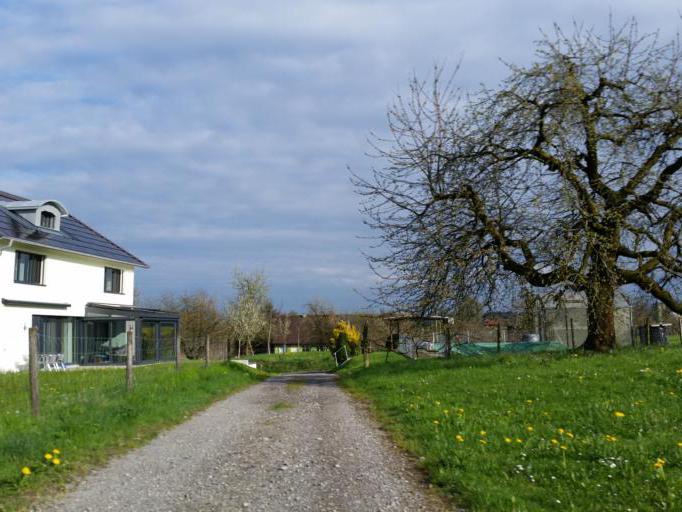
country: CH
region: Thurgau
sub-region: Arbon District
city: Uttwil
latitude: 47.5812
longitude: 9.3389
